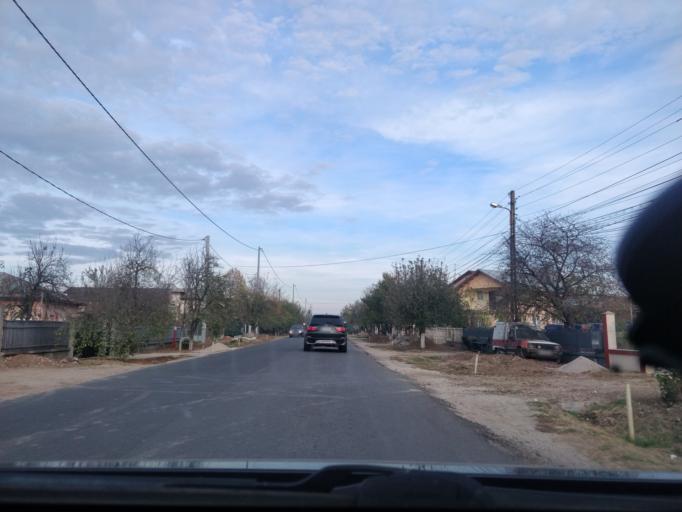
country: RO
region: Giurgiu
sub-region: Comuna Bolintin Vale
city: Malu Spart
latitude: 44.4408
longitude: 25.7067
